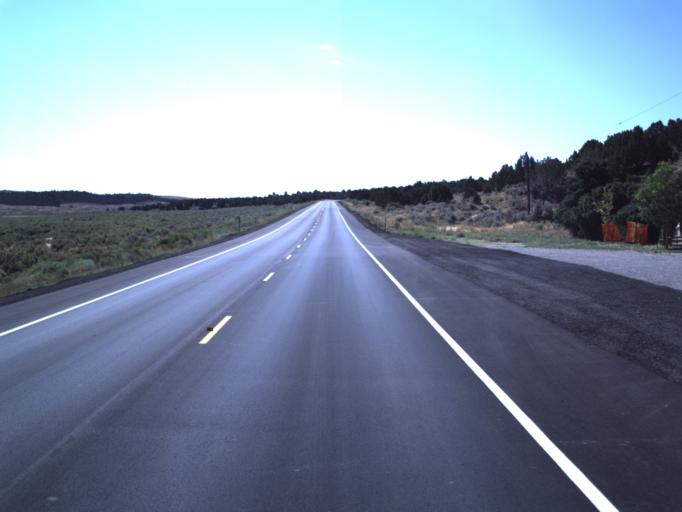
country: US
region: Utah
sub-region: Utah County
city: Eagle Mountain
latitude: 40.0167
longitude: -112.2787
